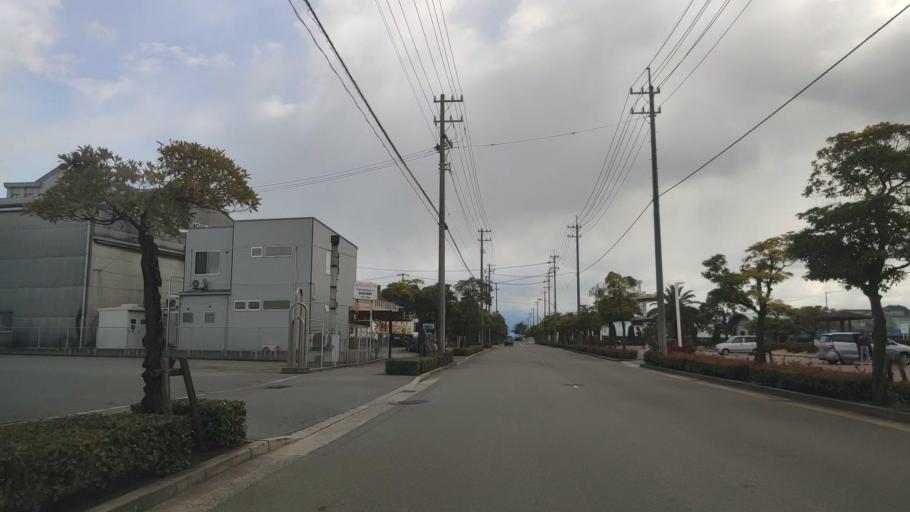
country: JP
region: Ehime
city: Saijo
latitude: 34.0487
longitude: 133.0264
